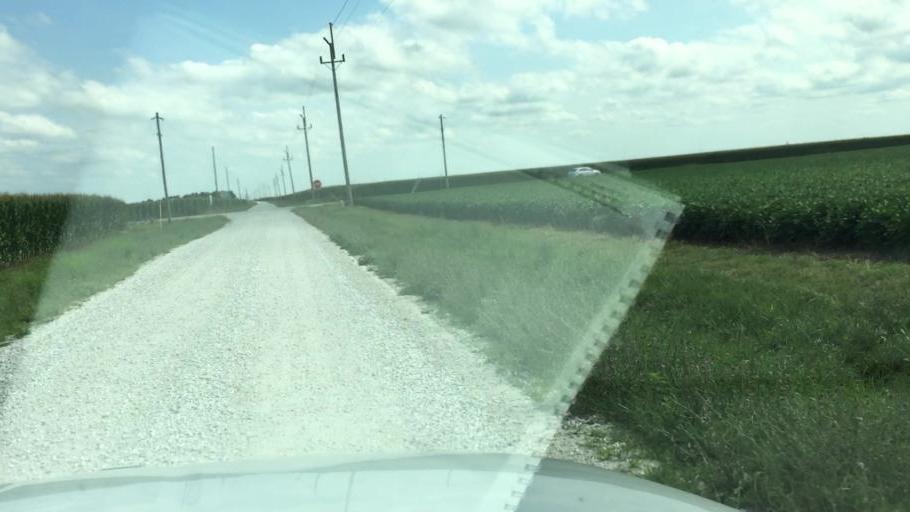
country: US
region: Illinois
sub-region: Hancock County
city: Carthage
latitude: 40.4070
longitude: -91.1787
